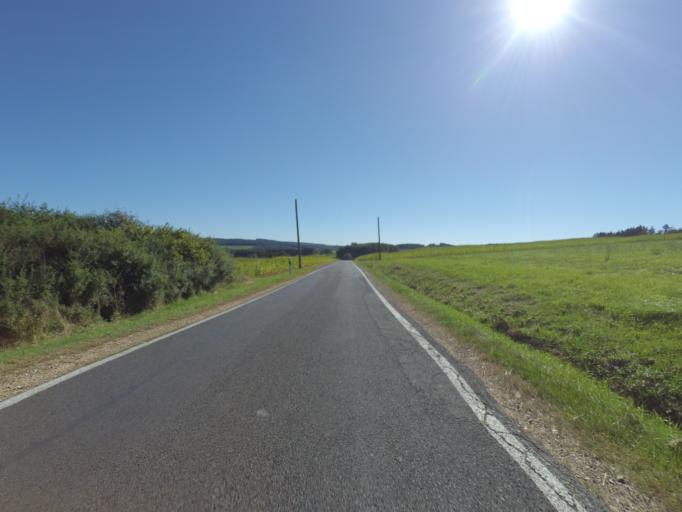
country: DE
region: Rheinland-Pfalz
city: Boxberg
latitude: 50.2521
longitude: 6.8802
